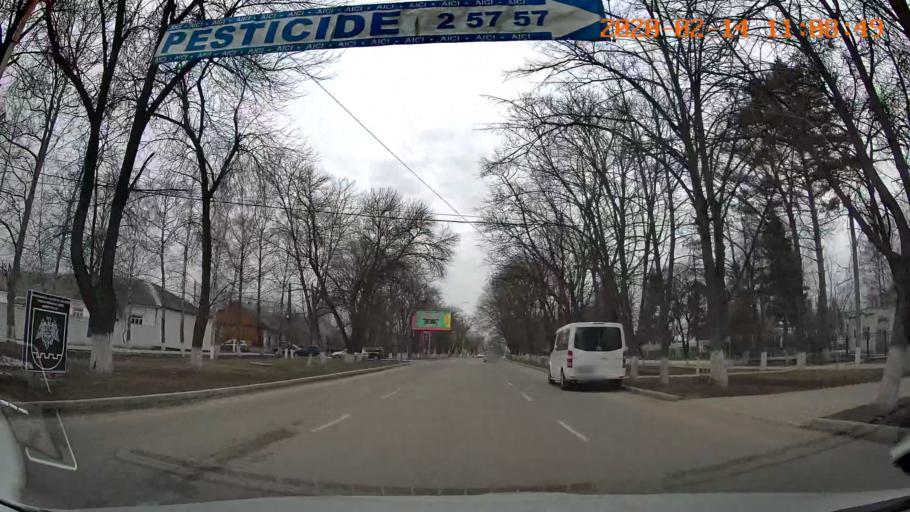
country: MD
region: Raionul Edinet
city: Edinet
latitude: 48.1743
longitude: 27.2987
